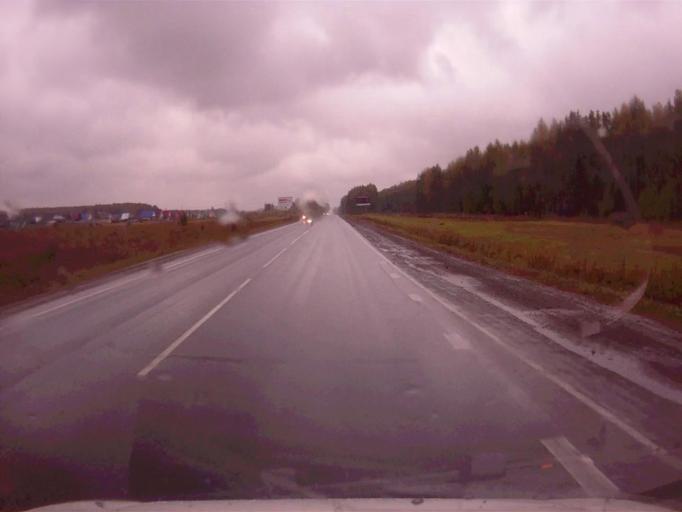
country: RU
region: Chelyabinsk
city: Argayash
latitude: 55.4195
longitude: 61.0196
